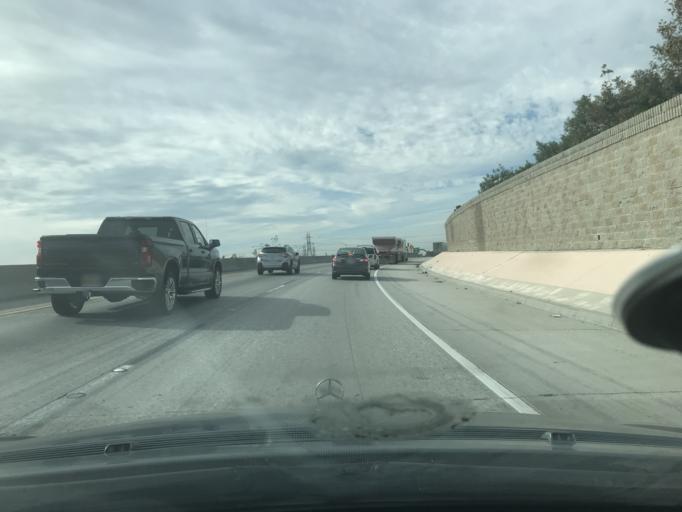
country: US
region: California
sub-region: Los Angeles County
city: Norwalk
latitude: 33.9151
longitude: -118.1068
